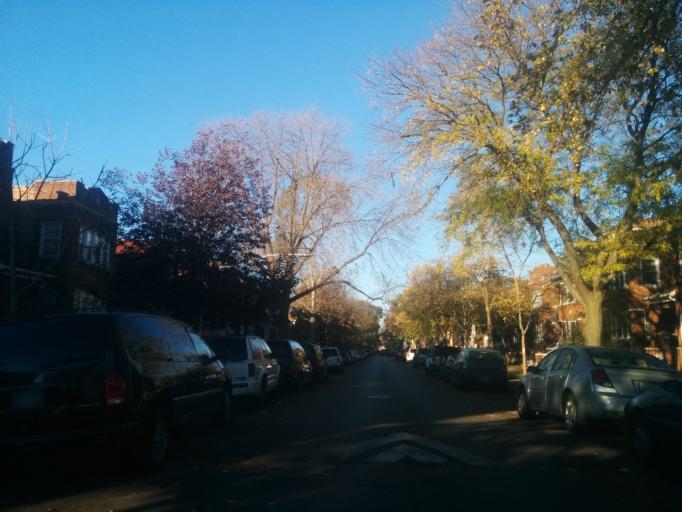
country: US
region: Illinois
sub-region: Cook County
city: Oak Park
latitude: 41.9269
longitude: -87.7570
